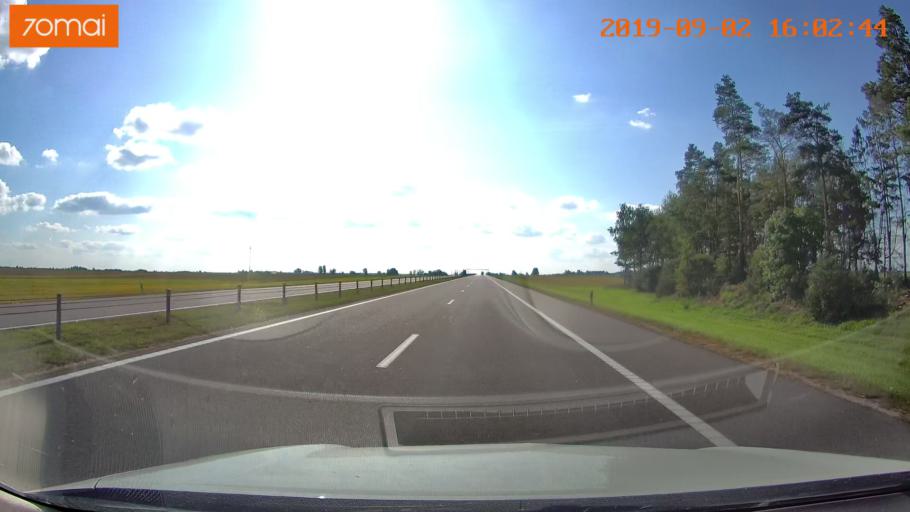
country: BY
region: Minsk
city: Byerazino
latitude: 53.8072
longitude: 28.8870
